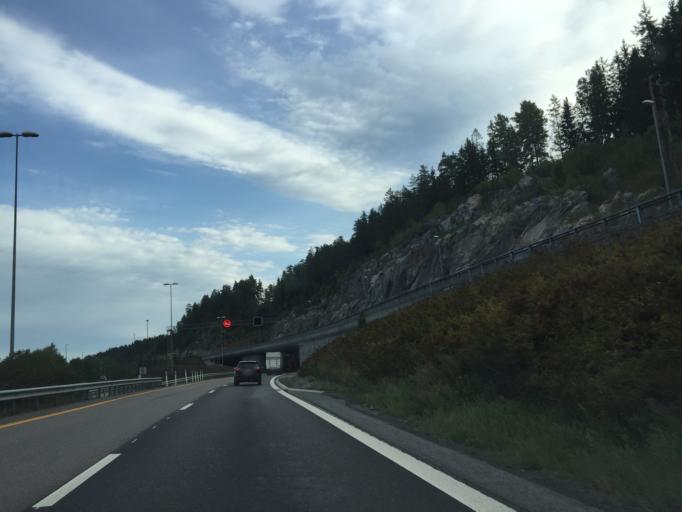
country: NO
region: Akershus
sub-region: Ski
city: Ski
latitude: 59.7503
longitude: 10.7839
